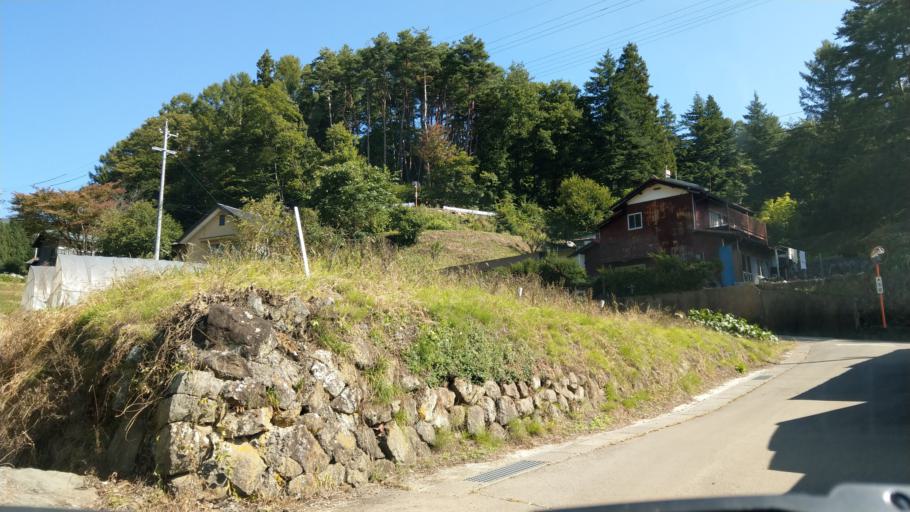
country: JP
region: Nagano
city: Komoro
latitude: 36.3572
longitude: 138.4313
